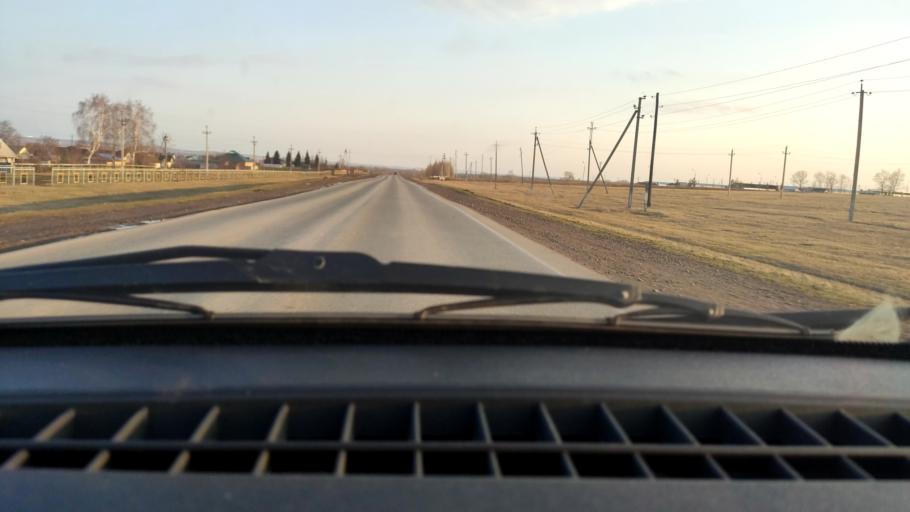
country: RU
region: Bashkortostan
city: Davlekanovo
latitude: 54.3805
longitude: 55.1956
